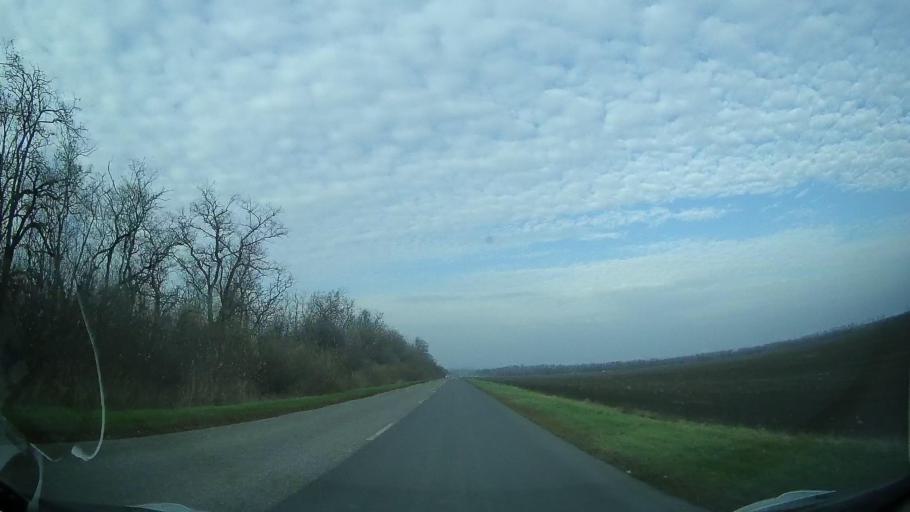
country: RU
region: Rostov
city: Bagayevskaya
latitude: 47.0845
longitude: 40.3915
